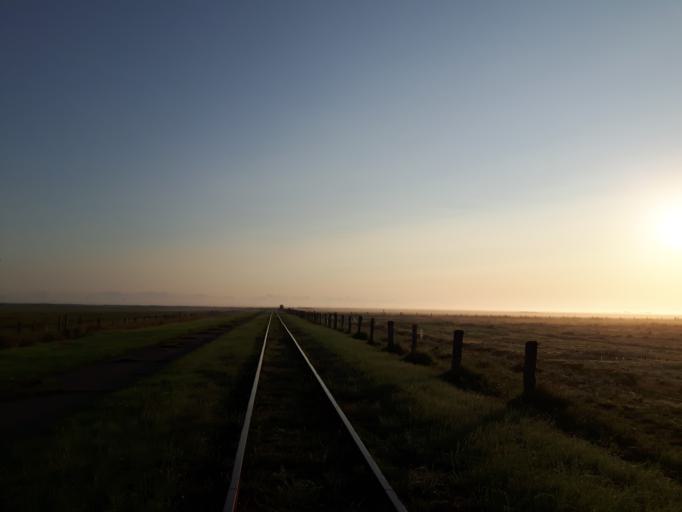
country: DE
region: Schleswig-Holstein
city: Grode
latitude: 54.6776
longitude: 8.7052
